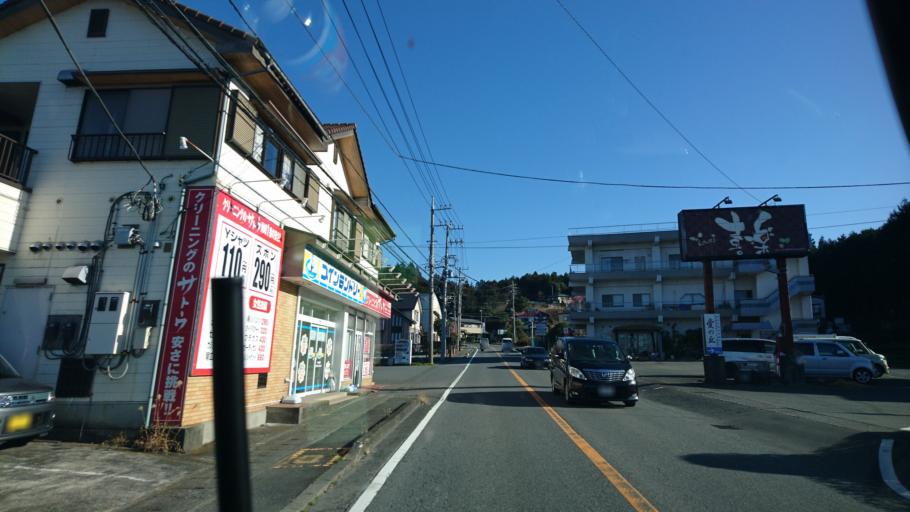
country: JP
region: Shizuoka
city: Fujinomiya
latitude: 35.2679
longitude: 138.6042
